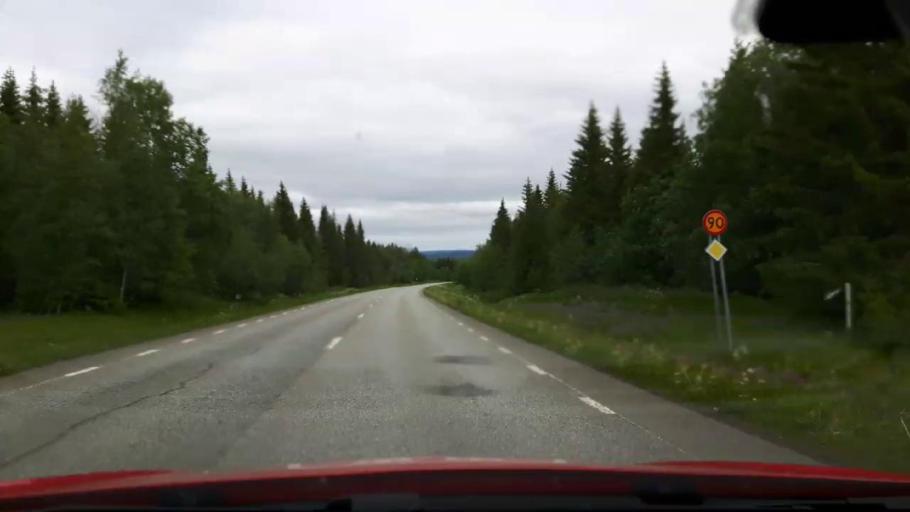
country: SE
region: Jaemtland
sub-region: Krokoms Kommun
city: Krokom
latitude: 63.5849
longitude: 14.6359
